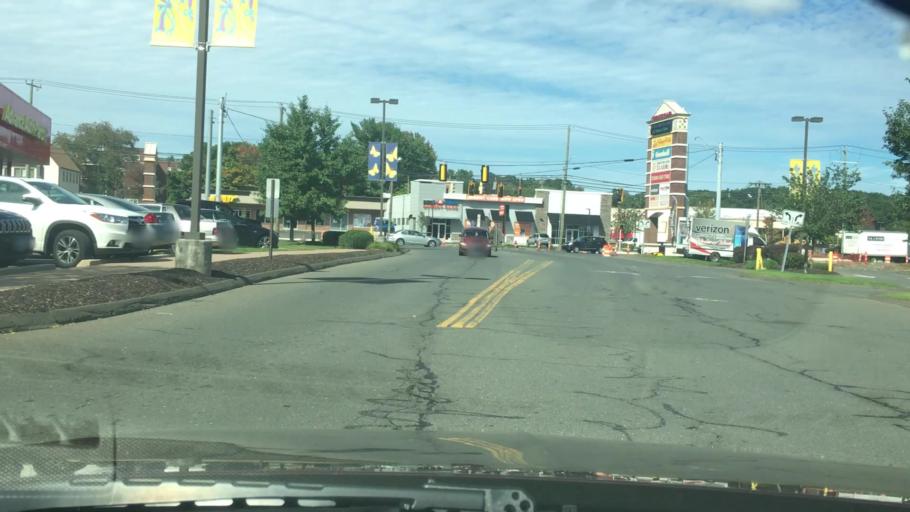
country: US
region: Connecticut
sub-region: Hartford County
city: Plainville
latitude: 41.6968
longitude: -72.9034
